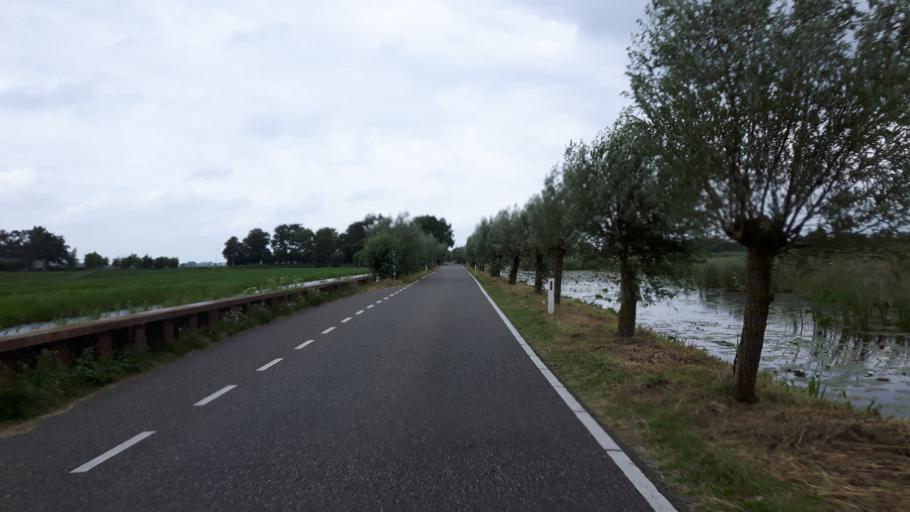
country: NL
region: South Holland
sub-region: Gemeente Nieuwkoop
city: Nieuwkoop
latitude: 52.1262
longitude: 4.7574
